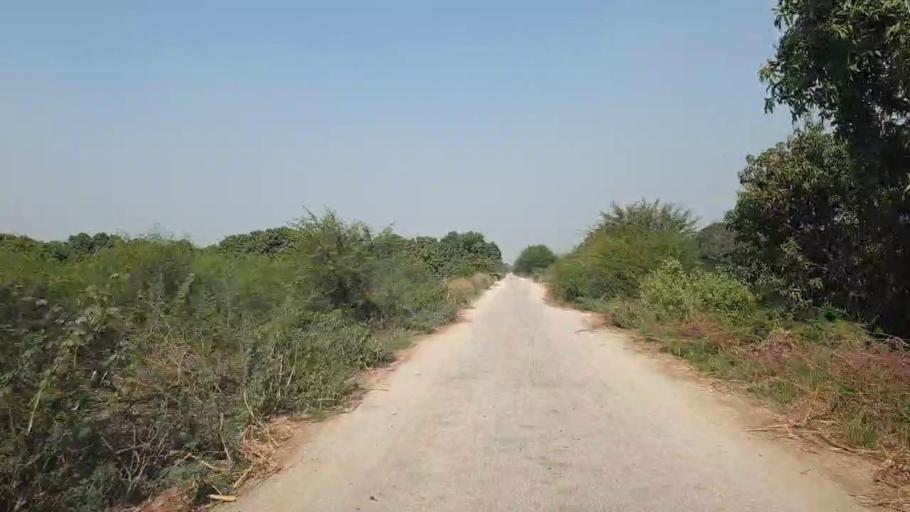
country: PK
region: Sindh
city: Chambar
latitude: 25.4049
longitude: 68.8878
